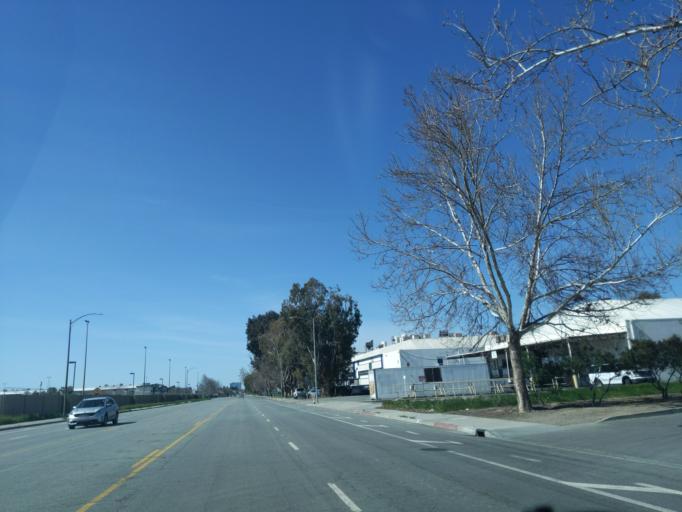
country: US
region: California
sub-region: Santa Clara County
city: Seven Trees
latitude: 37.3073
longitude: -121.8534
